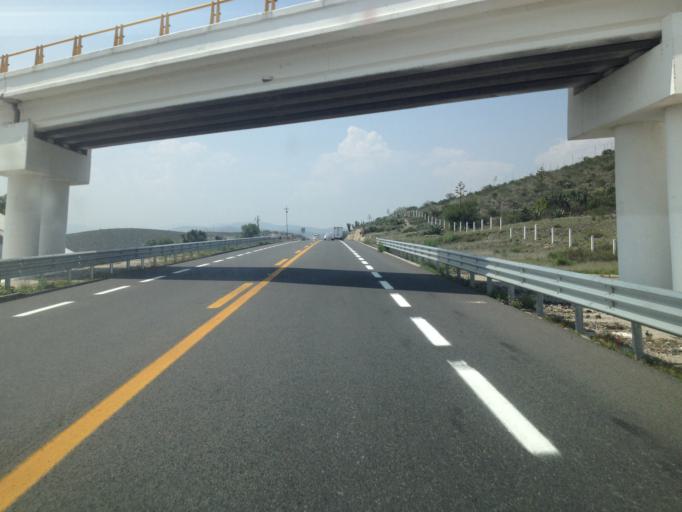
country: MX
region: Puebla
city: Cuacnopalan
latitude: 18.7934
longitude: -97.4891
